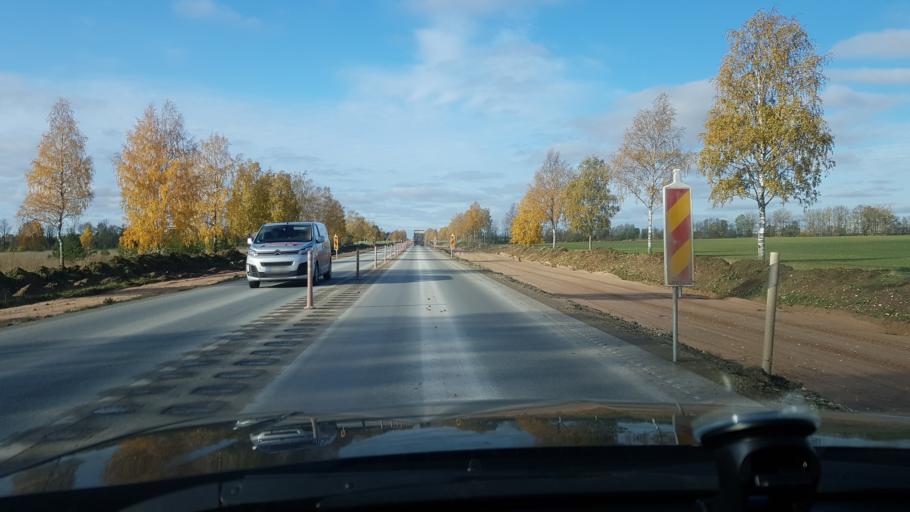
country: EE
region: Laeaene-Virumaa
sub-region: Haljala vald
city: Haljala
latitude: 59.4309
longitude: 26.2072
